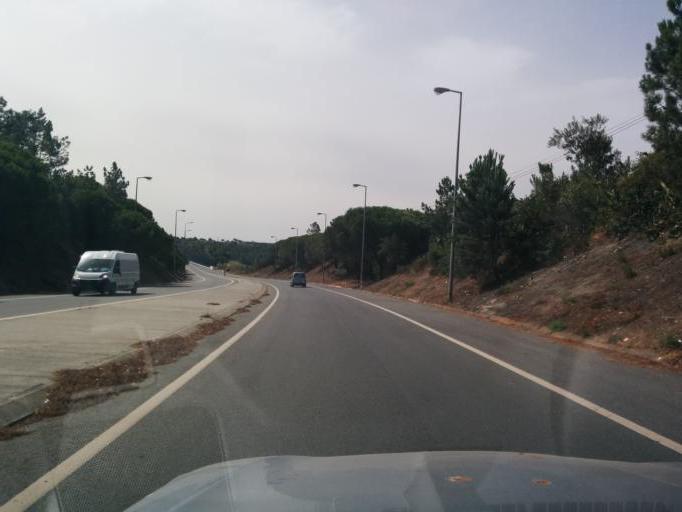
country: PT
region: Beja
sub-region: Odemira
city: Vila Nova de Milfontes
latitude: 37.7309
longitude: -8.7719
